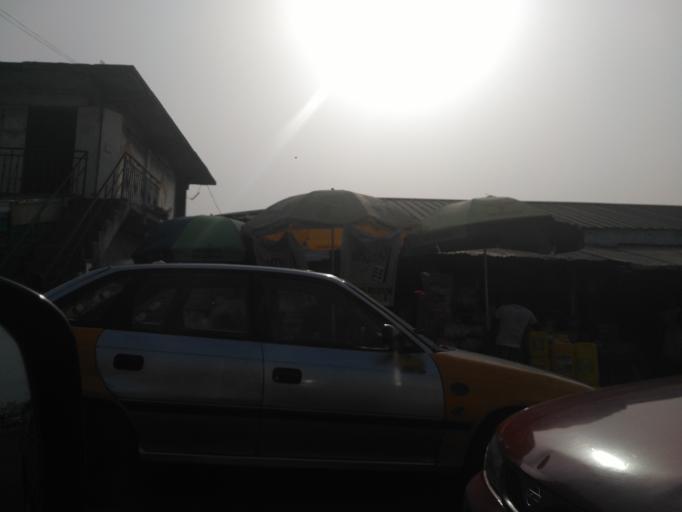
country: GH
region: Greater Accra
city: Accra
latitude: 5.5936
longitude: -0.1950
